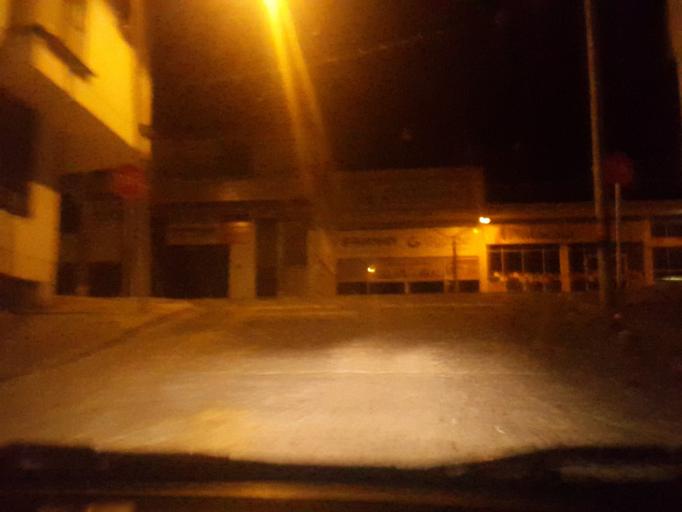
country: CO
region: Quindio
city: Armenia
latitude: 4.5365
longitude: -75.6761
